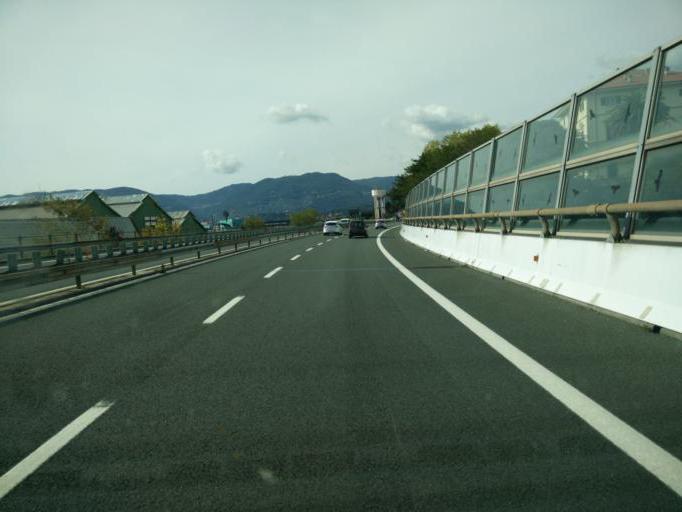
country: IT
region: Liguria
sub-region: Provincia di La Spezia
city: Pitelli
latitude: 44.1147
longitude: 9.8704
